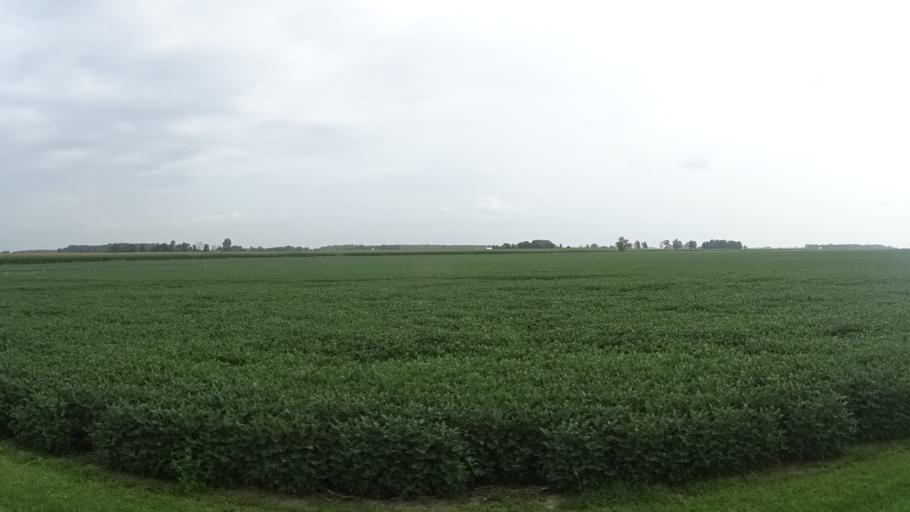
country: US
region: Indiana
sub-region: Madison County
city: Lapel
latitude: 40.0472
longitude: -85.8158
